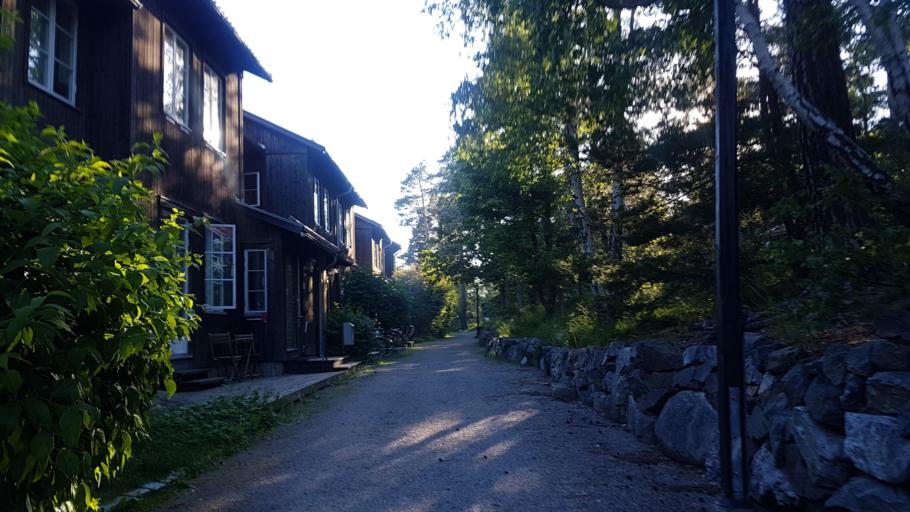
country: SE
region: Stockholm
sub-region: Nacka Kommun
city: Nacka
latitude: 59.2875
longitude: 18.1228
